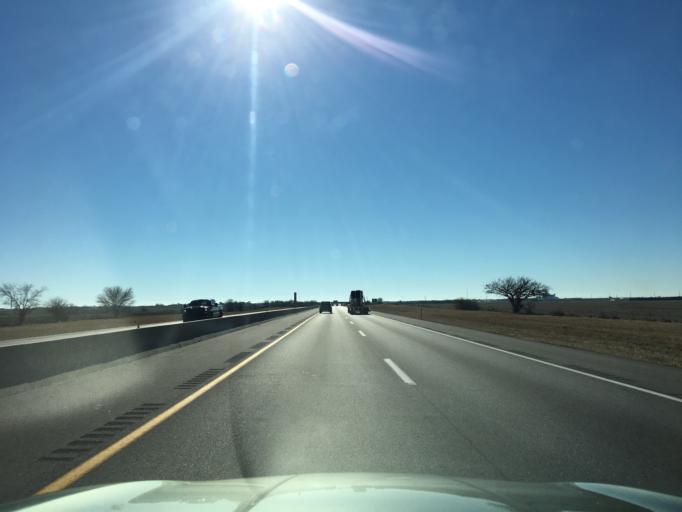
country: US
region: Kansas
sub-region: Sumner County
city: Wellington
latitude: 37.2976
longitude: -97.3404
